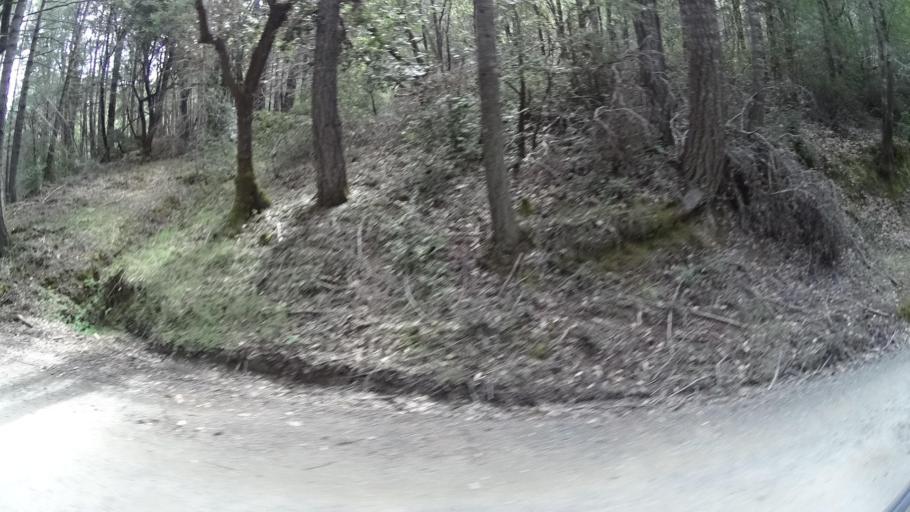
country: US
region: California
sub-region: Humboldt County
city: Redway
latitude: 40.0455
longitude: -123.8404
